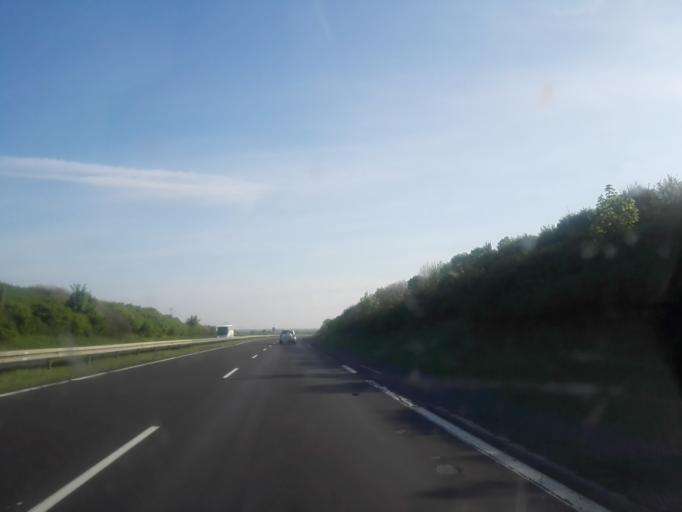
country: PL
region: Lodz Voivodeship
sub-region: Powiat radomszczanski
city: Kamiensk
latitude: 51.1946
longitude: 19.4743
